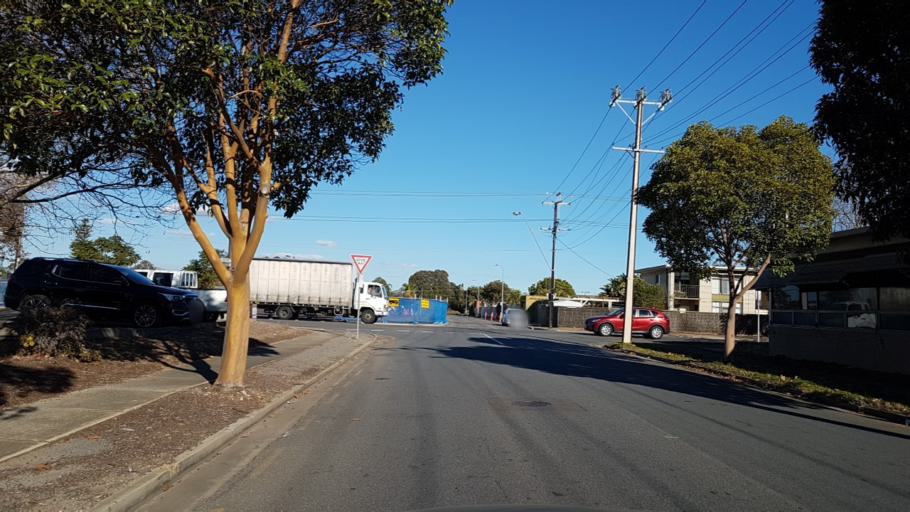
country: AU
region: South Australia
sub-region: City of West Torrens
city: Plympton
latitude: -34.9598
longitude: 138.5455
